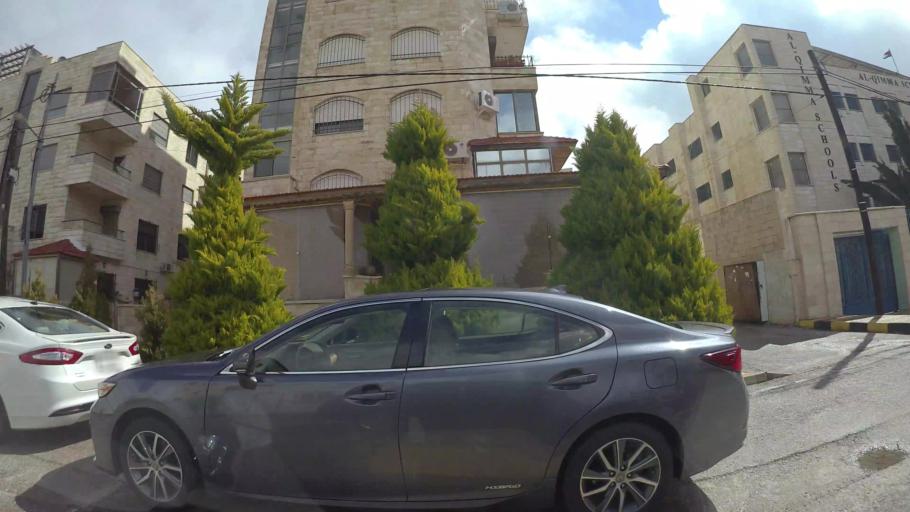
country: JO
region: Amman
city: Wadi as Sir
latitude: 31.9405
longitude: 35.8538
